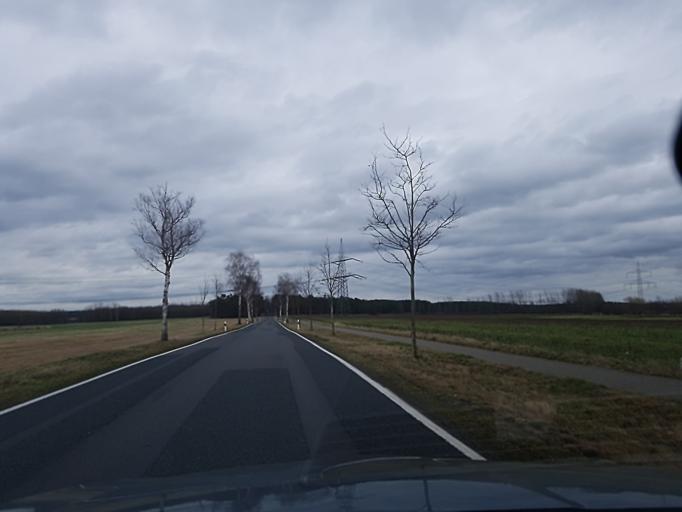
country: DE
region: Brandenburg
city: Bad Liebenwerda
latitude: 51.5571
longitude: 13.3918
